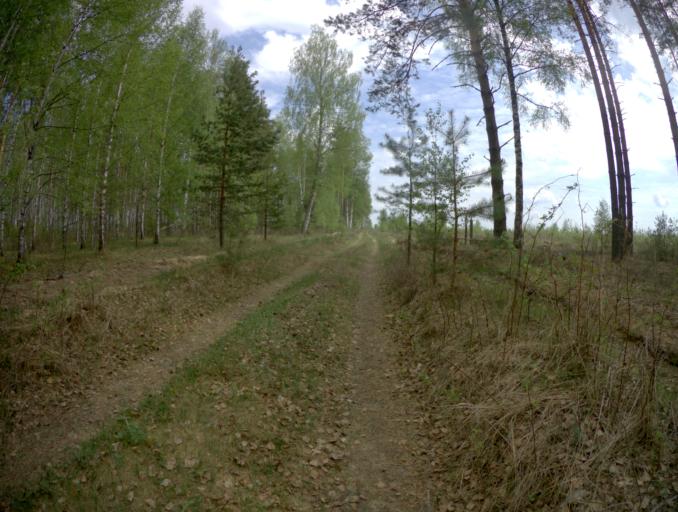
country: RU
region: Ivanovo
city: Talitsy
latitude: 56.4873
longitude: 42.1713
